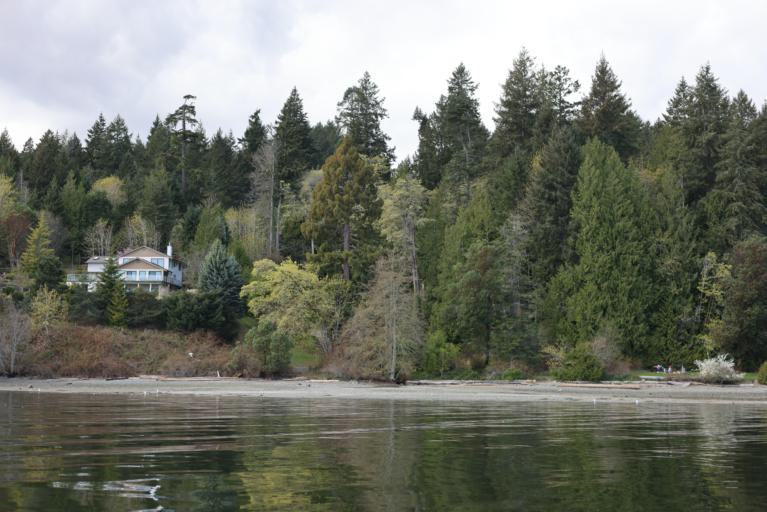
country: CA
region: British Columbia
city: North Saanich
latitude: 48.6043
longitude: -123.5192
